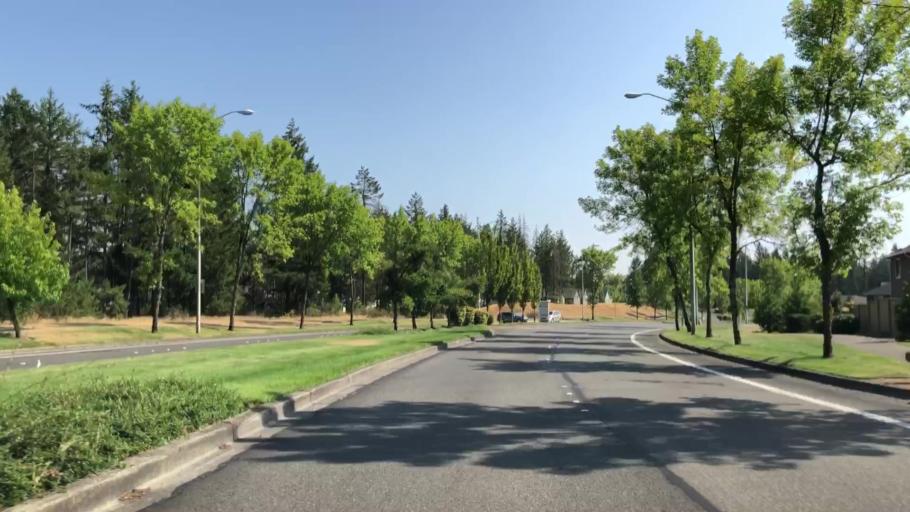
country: US
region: Washington
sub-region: Thurston County
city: Tanglewilde-Thompson Place
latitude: 47.0826
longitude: -122.7533
